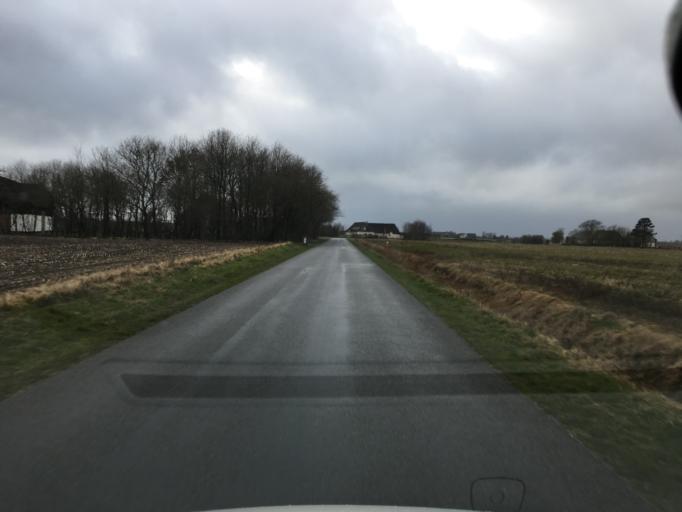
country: DE
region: Schleswig-Holstein
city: Bramstedtlund
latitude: 54.9380
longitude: 9.0702
